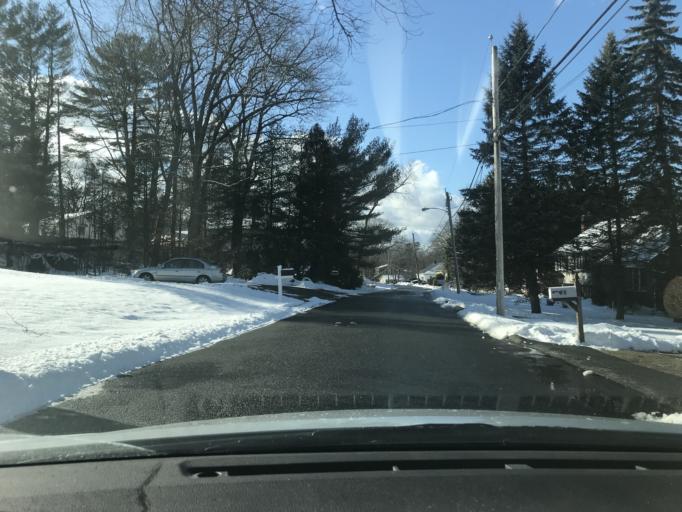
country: US
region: Massachusetts
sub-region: Essex County
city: Saugus
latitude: 42.4882
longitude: -71.0084
